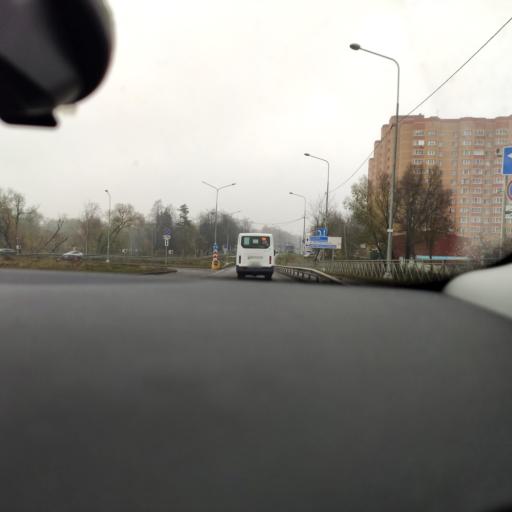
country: RU
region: Moskovskaya
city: Nakhabino
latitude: 55.8380
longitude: 37.1612
